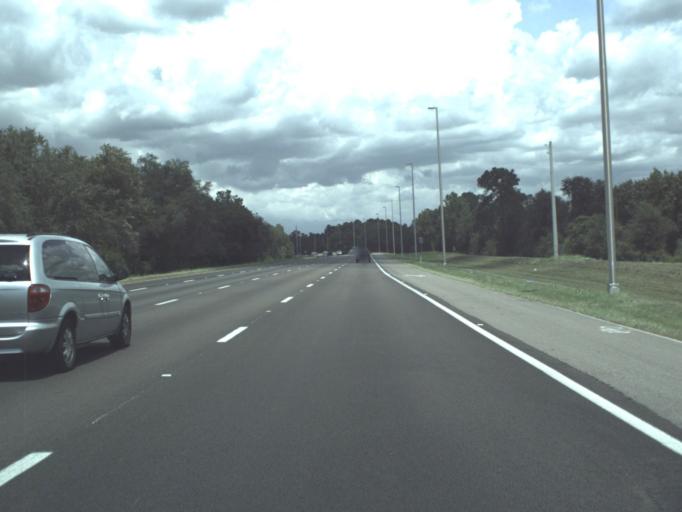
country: US
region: Florida
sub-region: Hillsborough County
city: Thonotosassa
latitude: 28.0818
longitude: -82.3530
